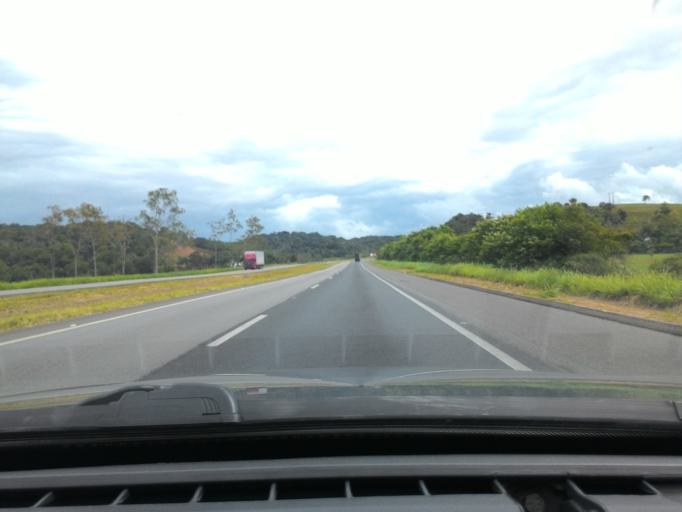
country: BR
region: Sao Paulo
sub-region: Registro
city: Registro
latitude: -24.5875
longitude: -47.8820
